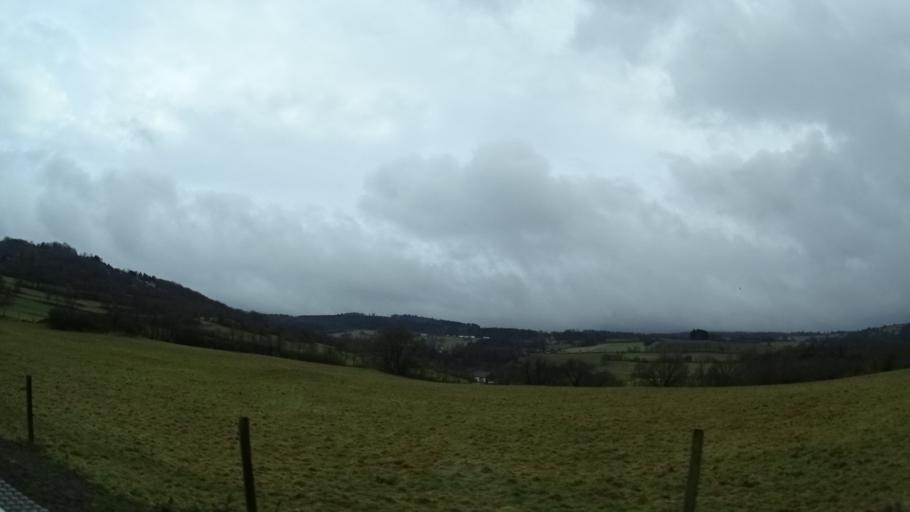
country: DE
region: Hesse
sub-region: Regierungsbezirk Giessen
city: Ulrichstein
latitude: 50.5809
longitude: 9.1738
